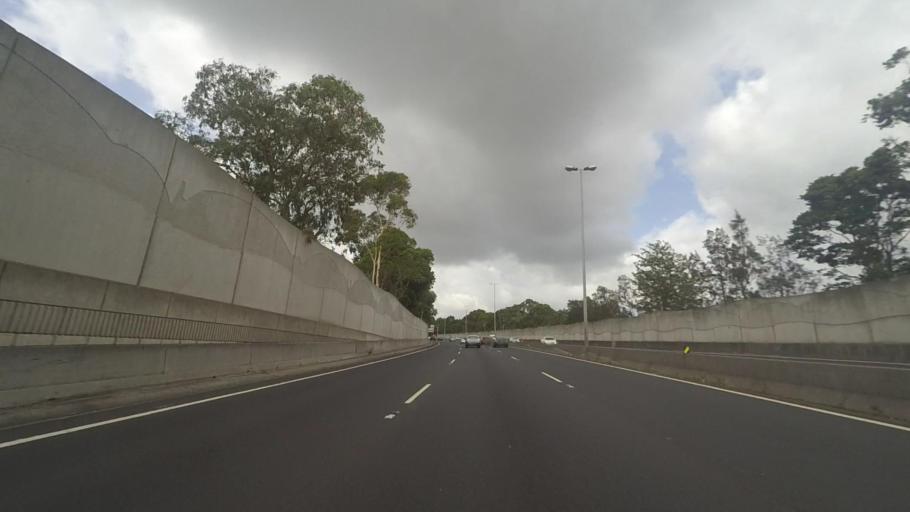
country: AU
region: New South Wales
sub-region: Wollongong
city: Keiraville
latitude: -34.4178
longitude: 150.8760
